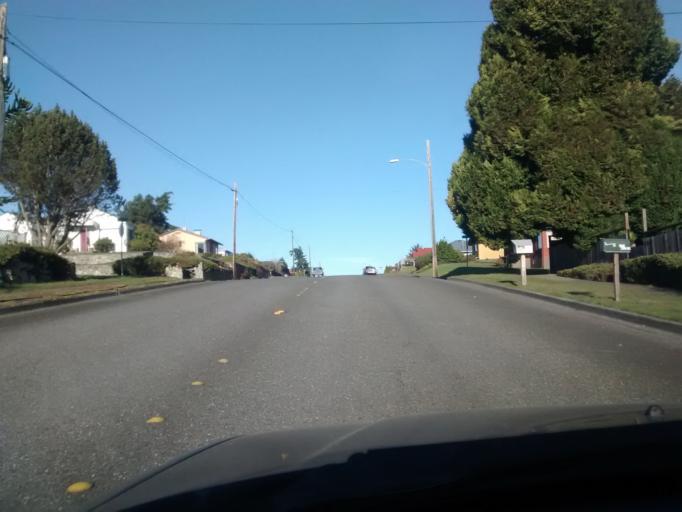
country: US
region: Washington
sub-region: Clallam County
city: Port Angeles
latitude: 48.1235
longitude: -123.4562
